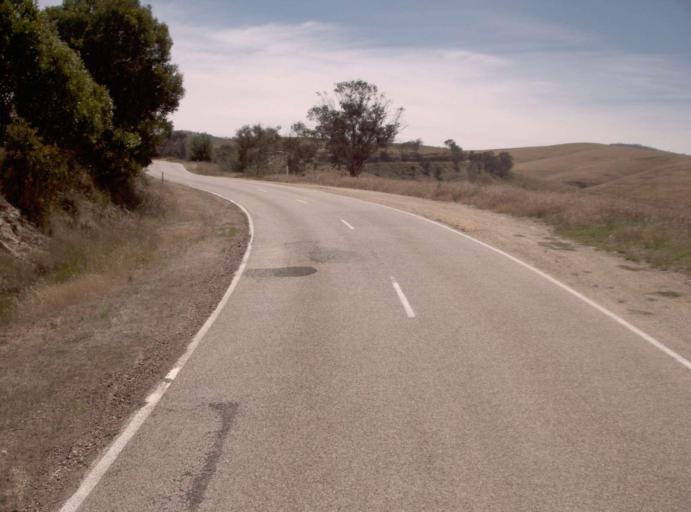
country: AU
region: Victoria
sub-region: Alpine
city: Mount Beauty
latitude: -37.0655
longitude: 147.6070
